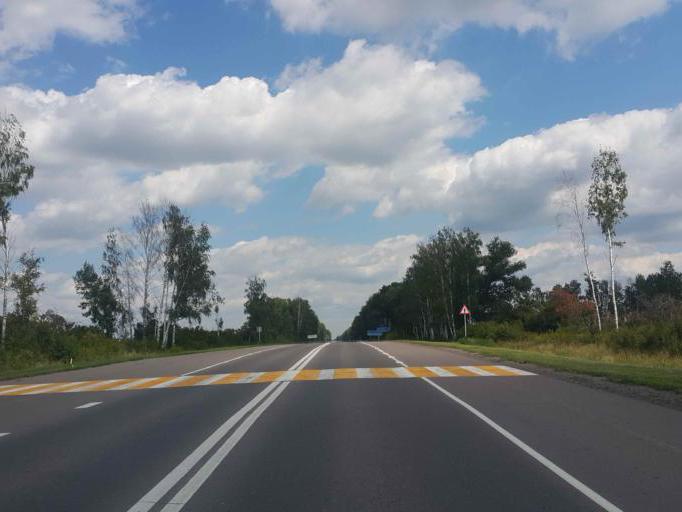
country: RU
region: Tambov
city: Goreloye
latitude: 53.0545
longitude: 41.4818
